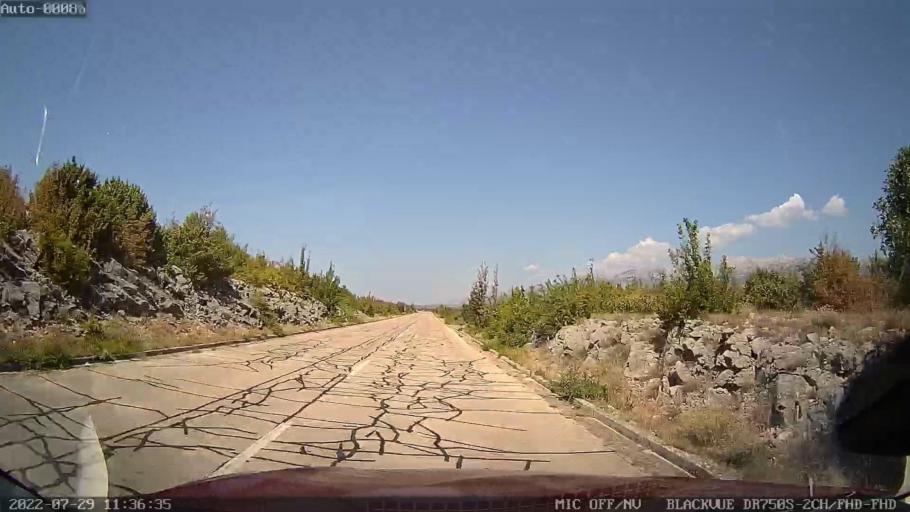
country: HR
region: Zadarska
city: Obrovac
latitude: 44.1904
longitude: 15.6960
